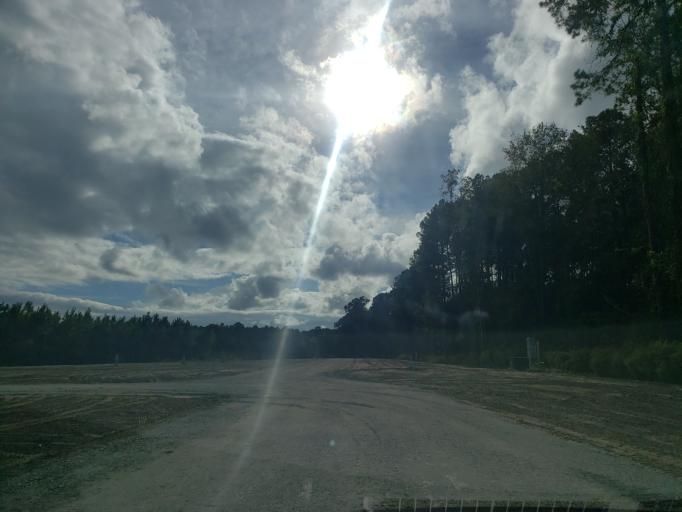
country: US
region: Georgia
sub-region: Bryan County
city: Richmond Hill
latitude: 32.0077
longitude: -81.2957
